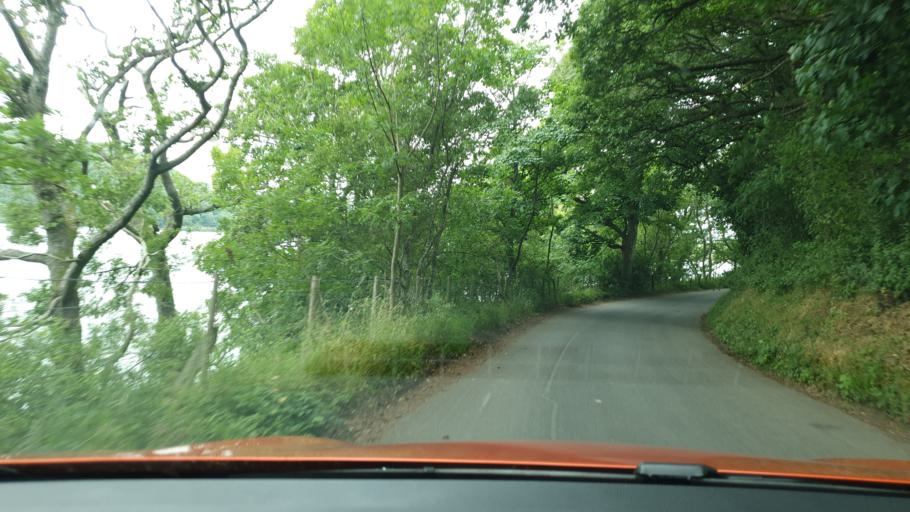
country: GB
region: England
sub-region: Cumbria
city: Penrith
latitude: 54.5982
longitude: -2.8356
